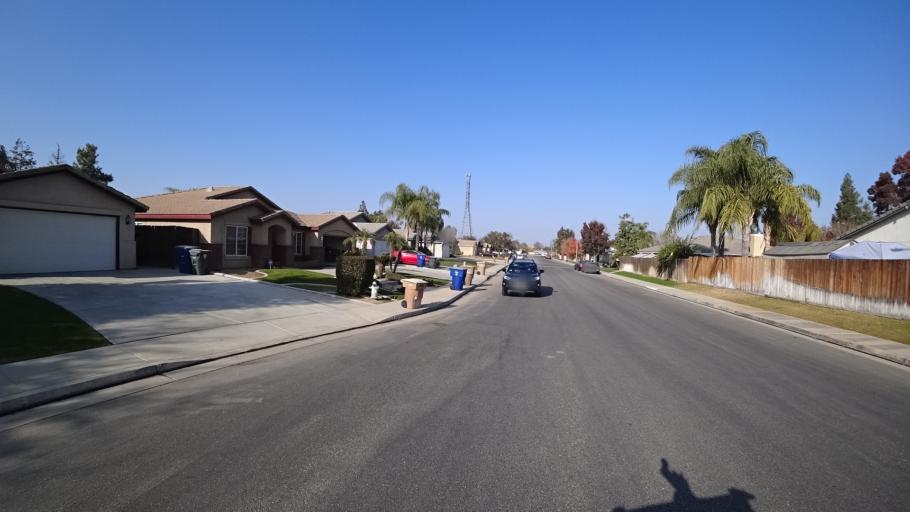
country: US
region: California
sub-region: Kern County
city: Greenacres
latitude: 35.3956
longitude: -119.0728
